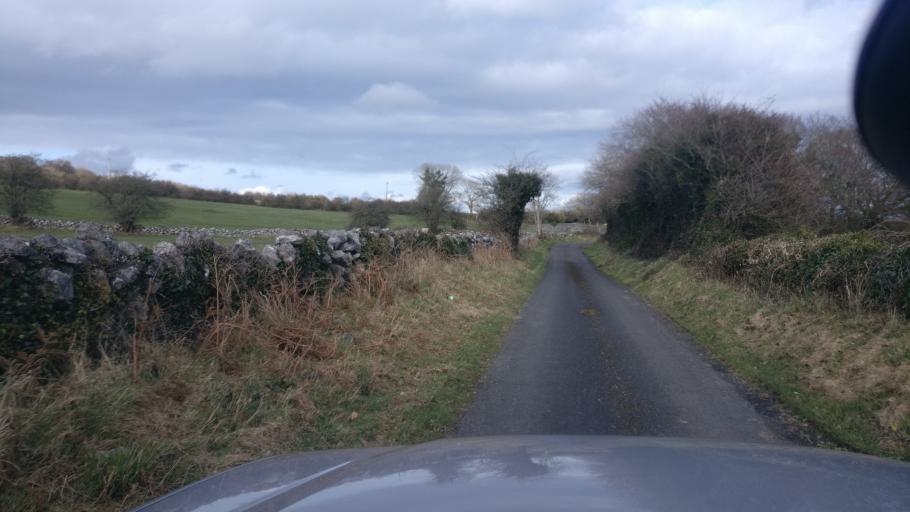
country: IE
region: Connaught
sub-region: County Galway
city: Loughrea
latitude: 53.1909
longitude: -8.4863
